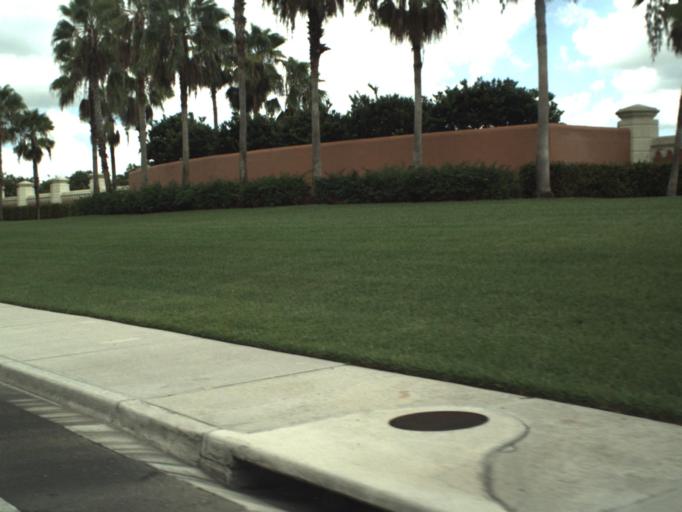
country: US
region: Florida
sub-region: Palm Beach County
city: Wellington
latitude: 26.6509
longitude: -80.1988
